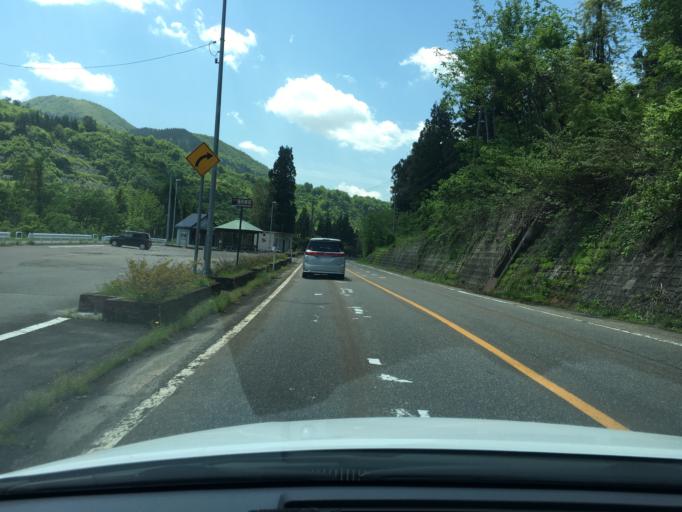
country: JP
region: Niigata
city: Tochio-honcho
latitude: 37.3085
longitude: 139.0109
